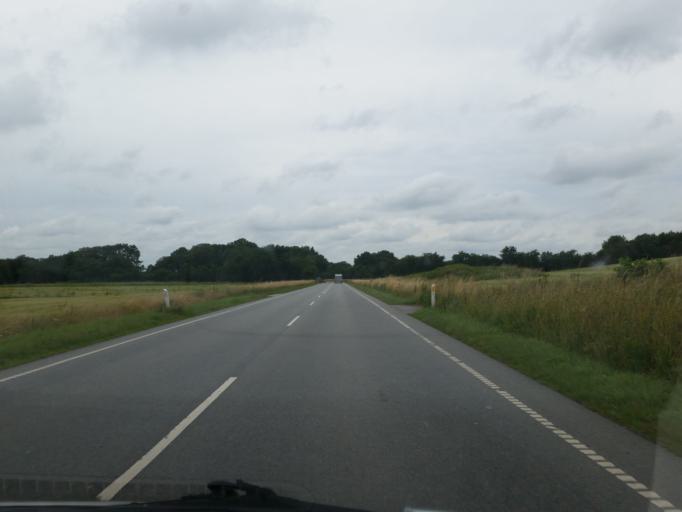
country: DK
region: South Denmark
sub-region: Vejen Kommune
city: Holsted
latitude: 55.4099
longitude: 8.9404
